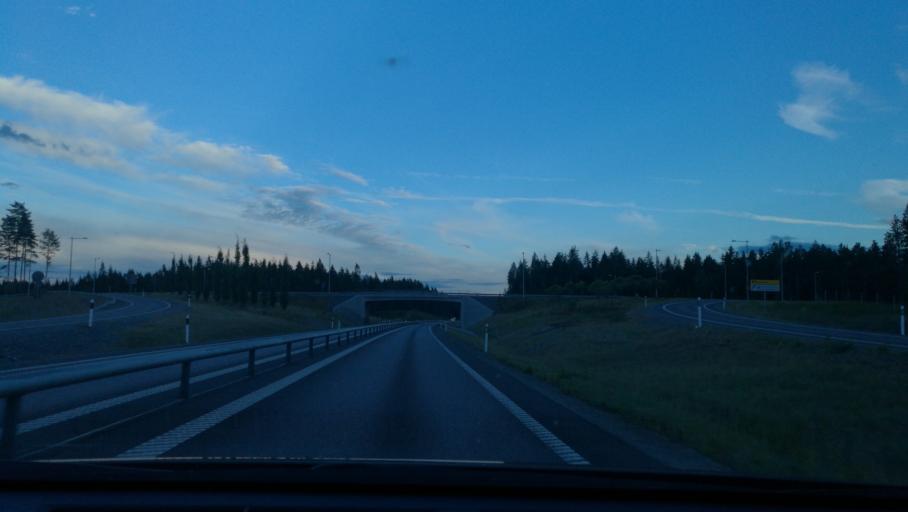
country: SE
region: Soedermanland
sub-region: Katrineholms Kommun
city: Katrineholm
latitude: 58.9950
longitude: 16.2584
